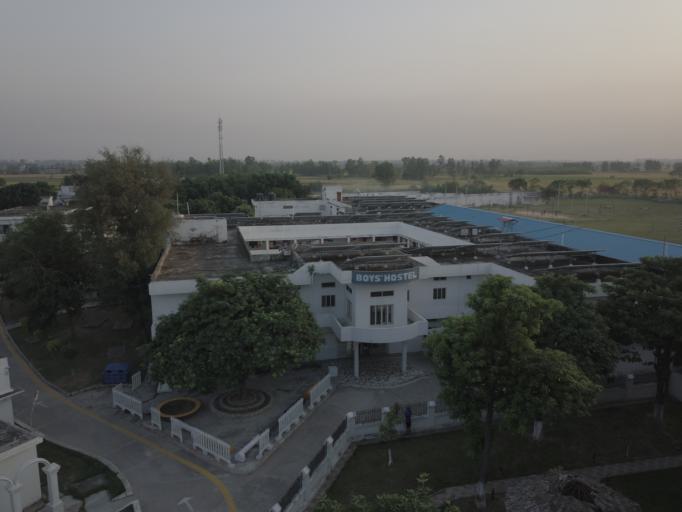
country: IN
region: Punjab
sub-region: Shahid Bhagat Singh Nagar
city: Rahon
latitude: 31.0205
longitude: 76.0887
